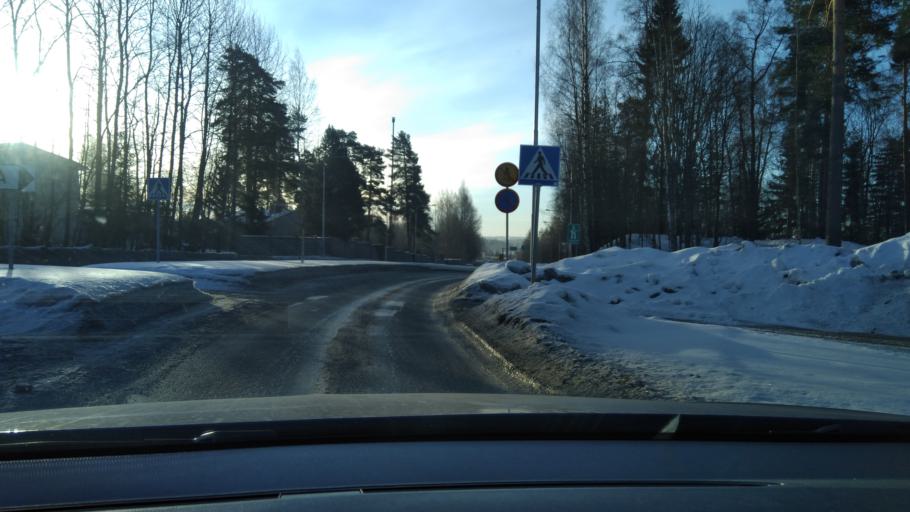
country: FI
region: Pirkanmaa
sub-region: Tampere
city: Pirkkala
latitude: 61.5006
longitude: 23.6482
